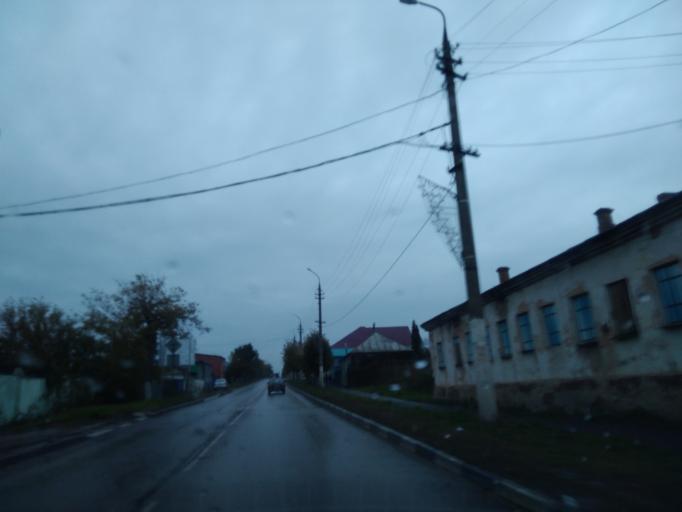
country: RU
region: Tula
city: Yefremov
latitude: 53.1378
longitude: 38.1168
